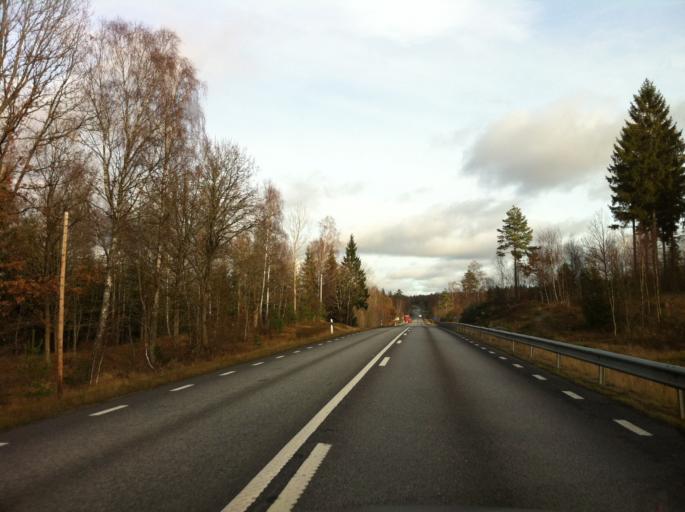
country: SE
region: Kronoberg
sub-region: Alvesta Kommun
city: Vislanda
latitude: 56.7733
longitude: 14.5418
